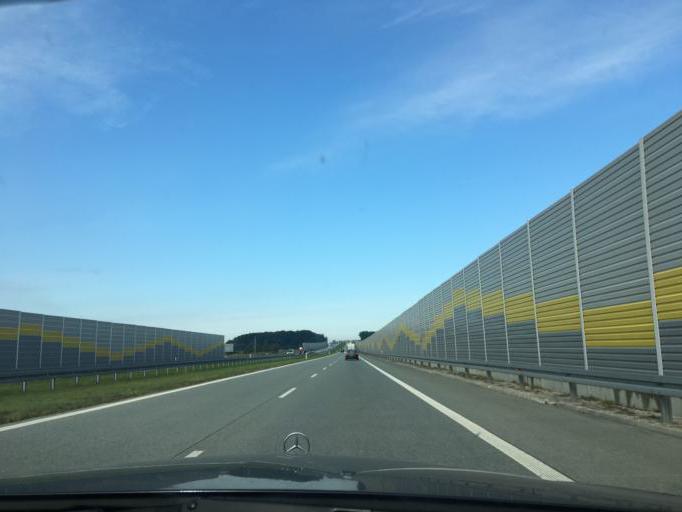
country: PL
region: Lodz Voivodeship
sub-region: Powiat laski
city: Sedziejowice
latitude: 51.5615
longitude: 19.0007
